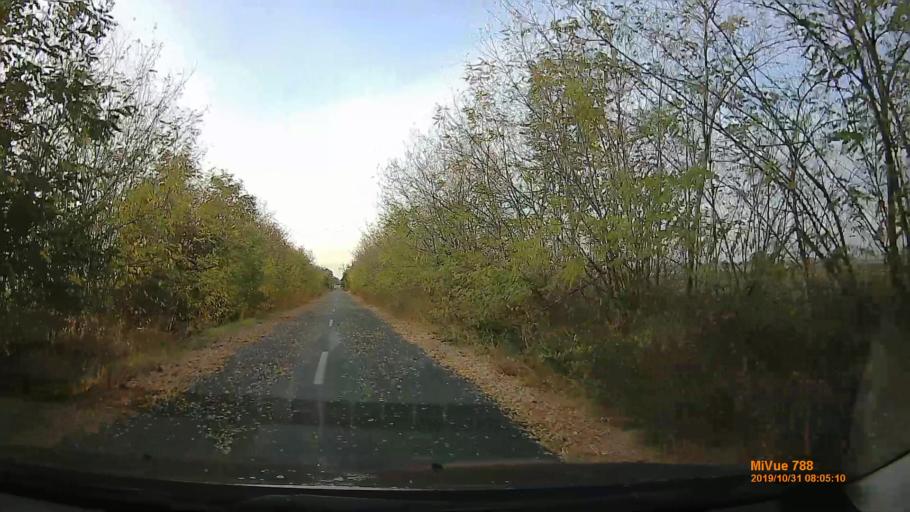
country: HU
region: Pest
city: Pilis
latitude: 47.3103
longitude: 19.5635
